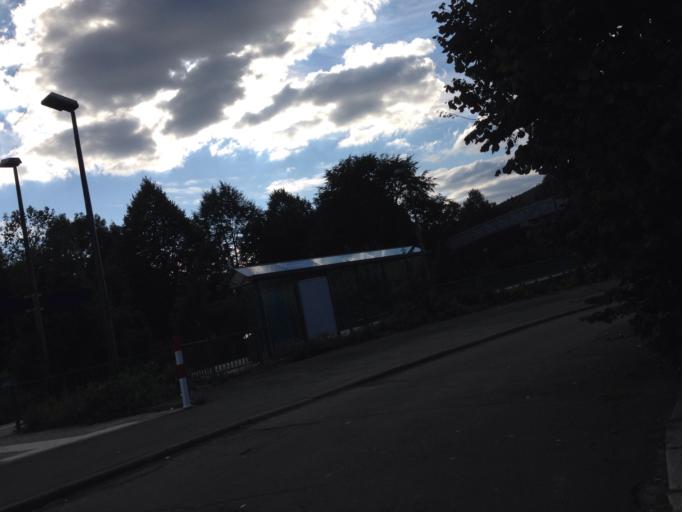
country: DE
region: Hesse
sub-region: Regierungsbezirk Giessen
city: Biedenkopf
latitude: 50.9152
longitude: 8.5181
